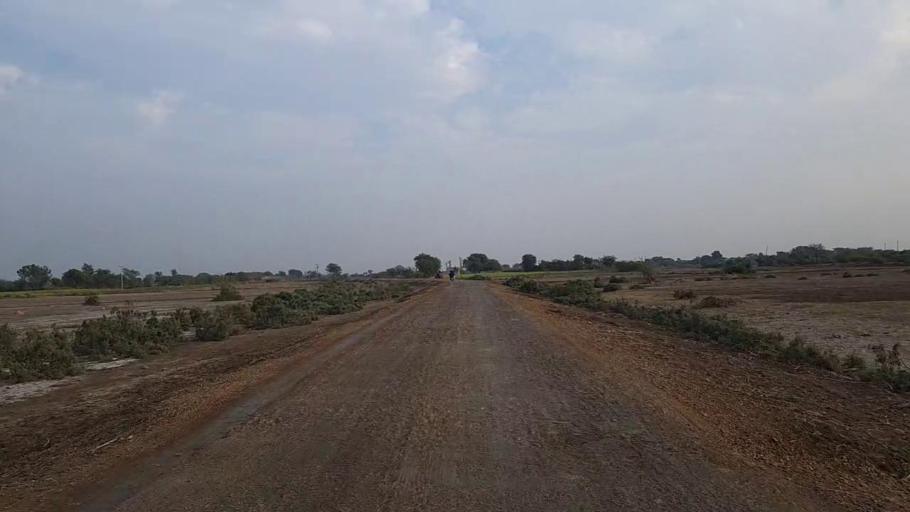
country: PK
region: Sindh
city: Pithoro
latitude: 25.4304
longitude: 69.3123
